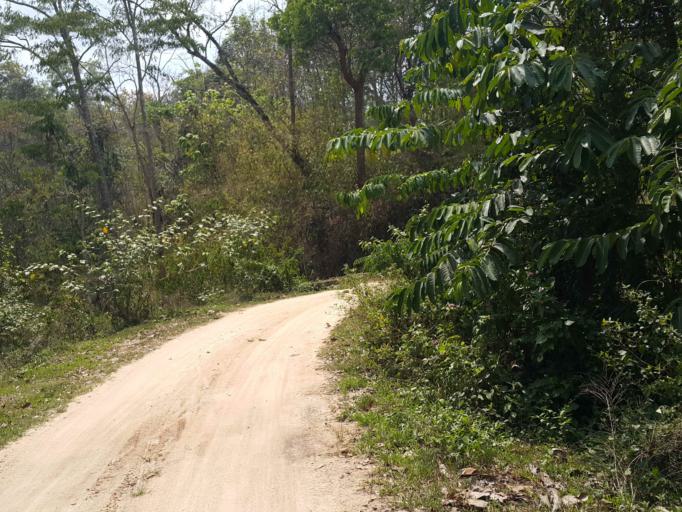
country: TH
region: Chiang Mai
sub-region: Amphoe Chiang Dao
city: Chiang Dao
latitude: 19.3018
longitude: 98.7469
